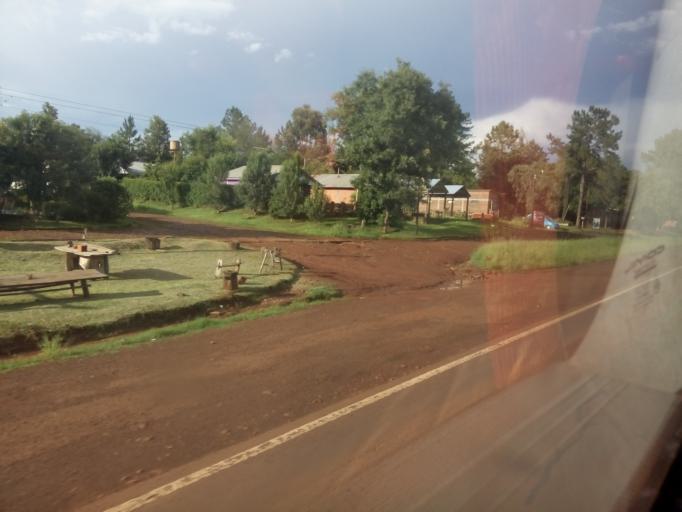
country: AR
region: Misiones
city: Santa Ana
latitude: -27.3818
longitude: -55.5839
